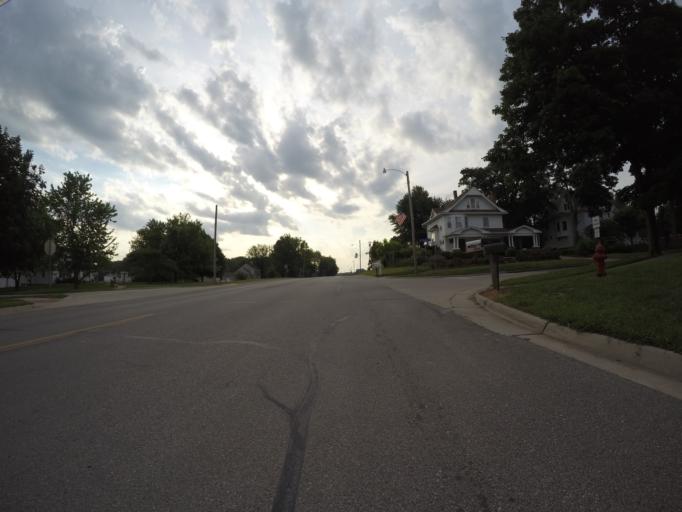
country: US
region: Kansas
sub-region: Doniphan County
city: Troy
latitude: 39.7898
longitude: -95.0885
